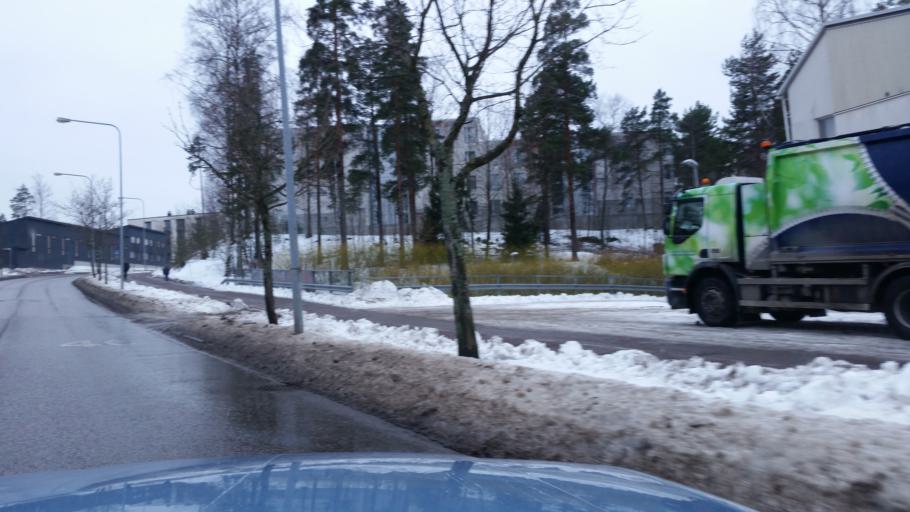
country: FI
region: Uusimaa
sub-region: Helsinki
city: Vantaa
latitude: 60.2332
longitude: 25.0622
